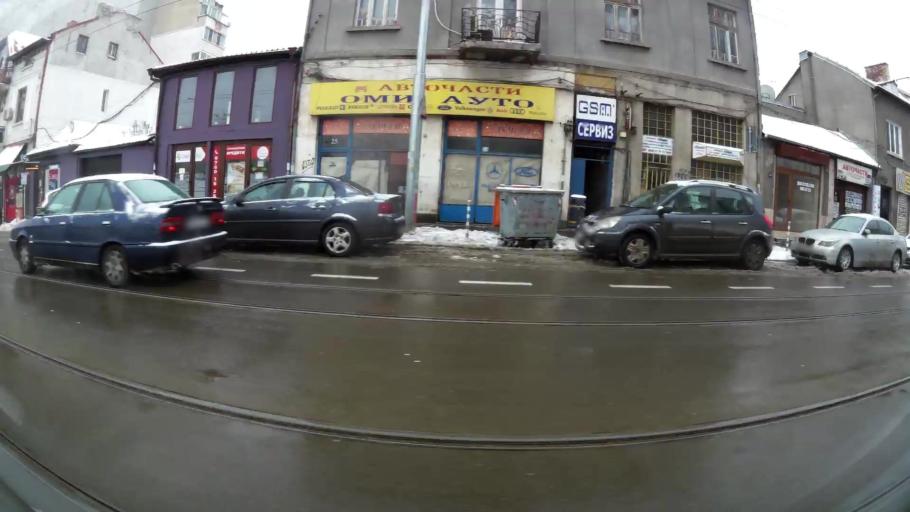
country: BG
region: Sofia-Capital
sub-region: Stolichna Obshtina
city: Sofia
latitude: 42.7078
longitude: 23.3291
